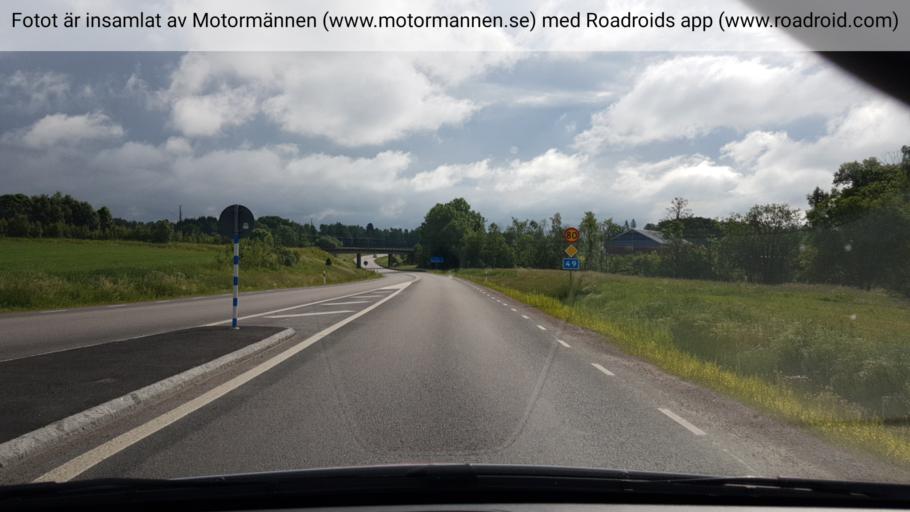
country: SE
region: Vaestra Goetaland
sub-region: Skovde Kommun
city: Skoevde
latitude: 58.3974
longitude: 13.9268
